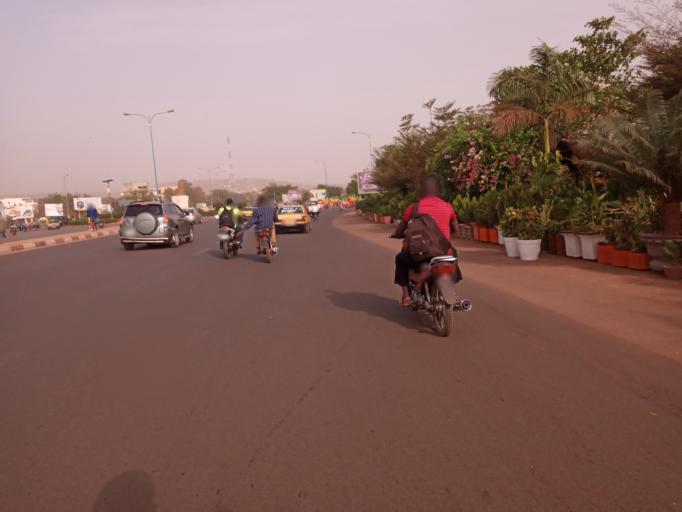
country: ML
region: Bamako
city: Bamako
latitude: 12.6365
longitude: -8.0158
